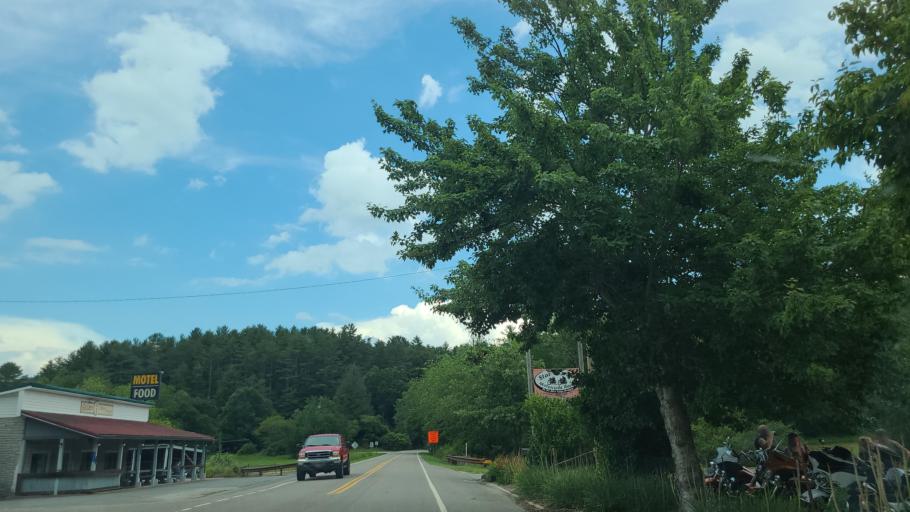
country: US
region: North Carolina
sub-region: Wilkes County
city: Mulberry
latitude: 36.3930
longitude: -81.2465
